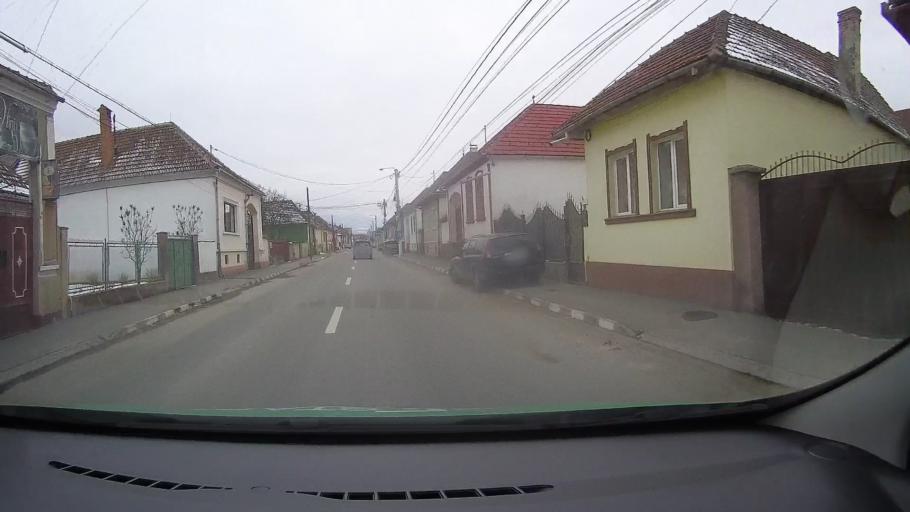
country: RO
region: Brasov
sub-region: Oras Rasnov
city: Rasnov
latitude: 45.5810
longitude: 25.4583
